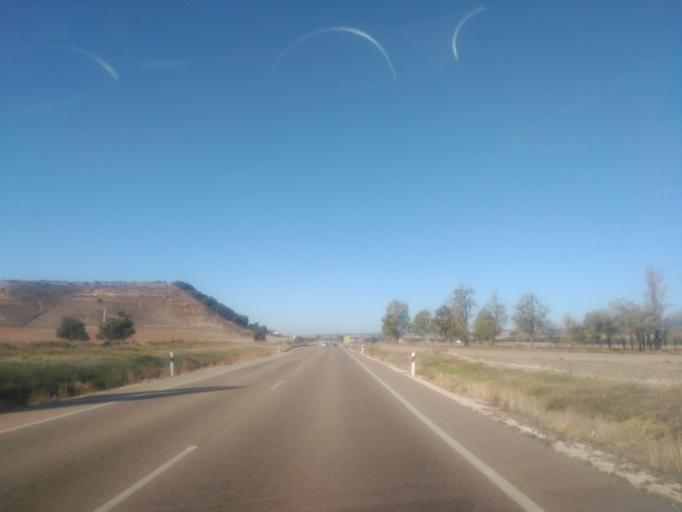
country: ES
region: Castille and Leon
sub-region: Provincia de Valladolid
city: Quintanilla de Arriba
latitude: 41.6160
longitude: -4.1942
